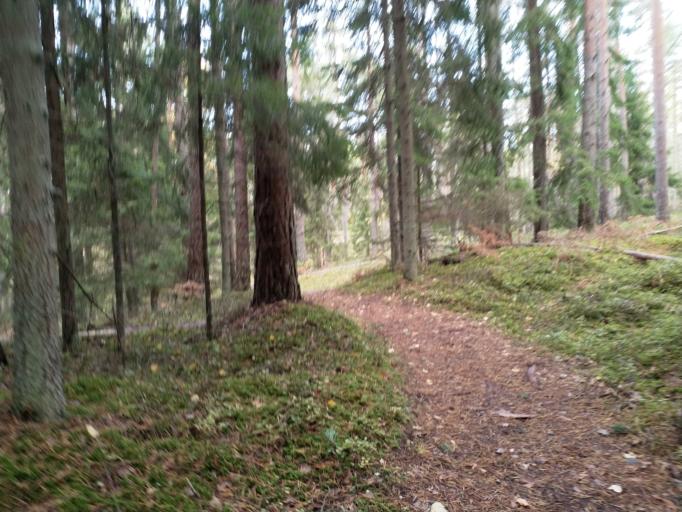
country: LV
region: Dundaga
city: Dundaga
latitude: 57.6477
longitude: 22.2593
